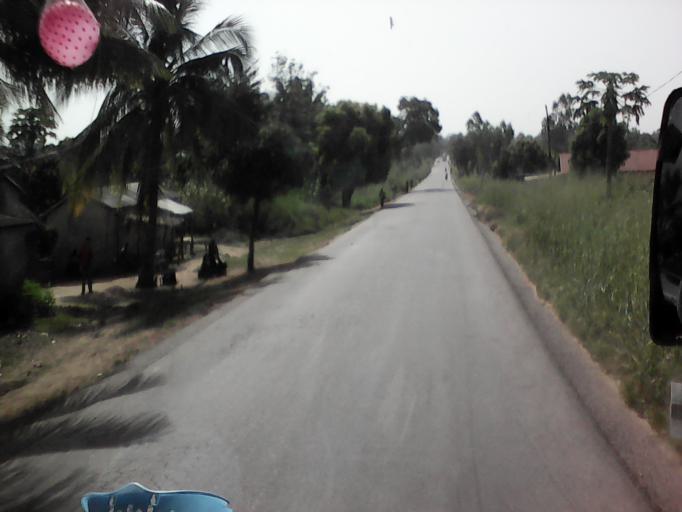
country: TG
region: Centrale
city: Sokode
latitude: 8.8373
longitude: 1.0759
